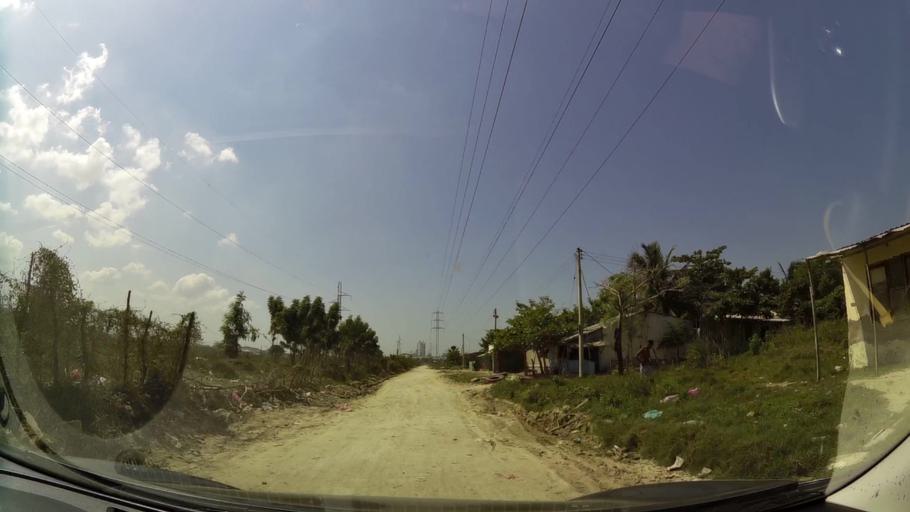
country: CO
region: Bolivar
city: Cartagena
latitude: 10.3540
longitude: -75.4843
